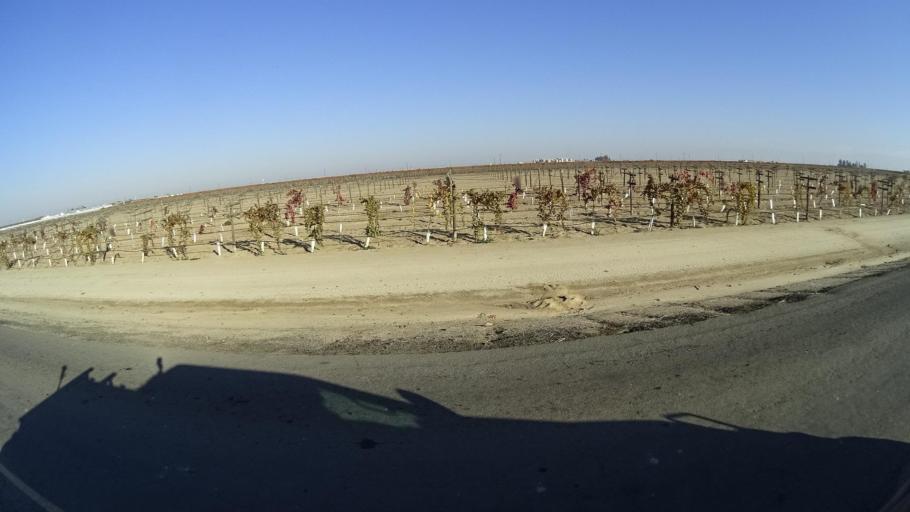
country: US
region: California
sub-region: Kern County
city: Delano
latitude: 35.7686
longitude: -119.1949
